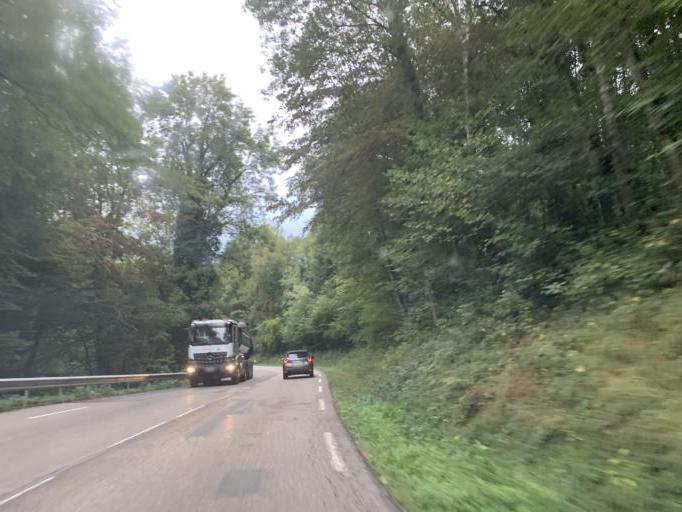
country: FR
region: Rhone-Alpes
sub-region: Departement de l'Ain
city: Belley
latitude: 45.7351
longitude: 5.6706
